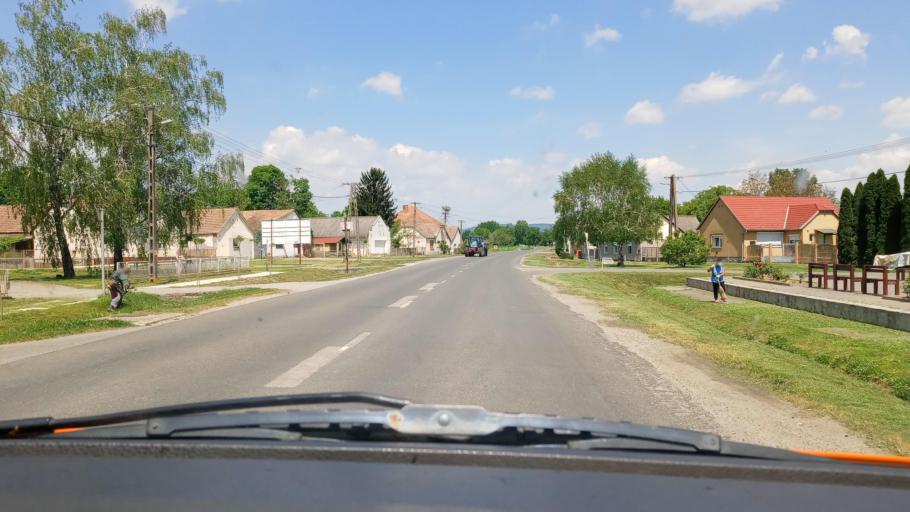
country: HU
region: Baranya
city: Harkany
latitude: 45.8078
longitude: 18.2119
